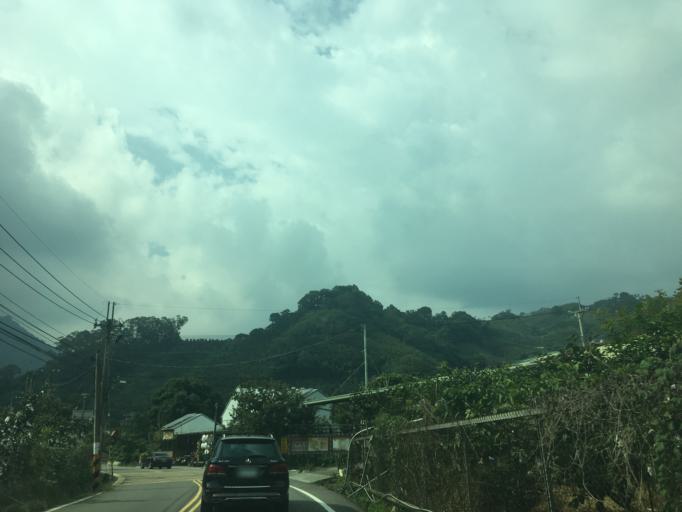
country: TW
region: Taiwan
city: Fengyuan
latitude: 24.3246
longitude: 120.9216
